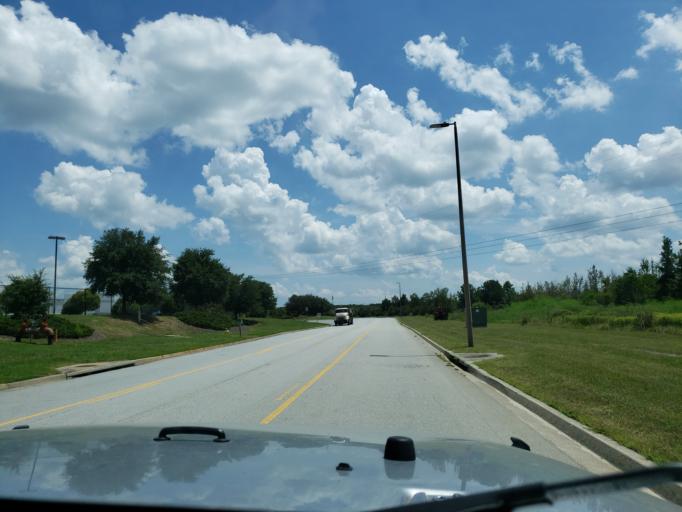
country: US
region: Georgia
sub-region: Chatham County
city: Pooler
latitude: 32.1065
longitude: -81.2738
